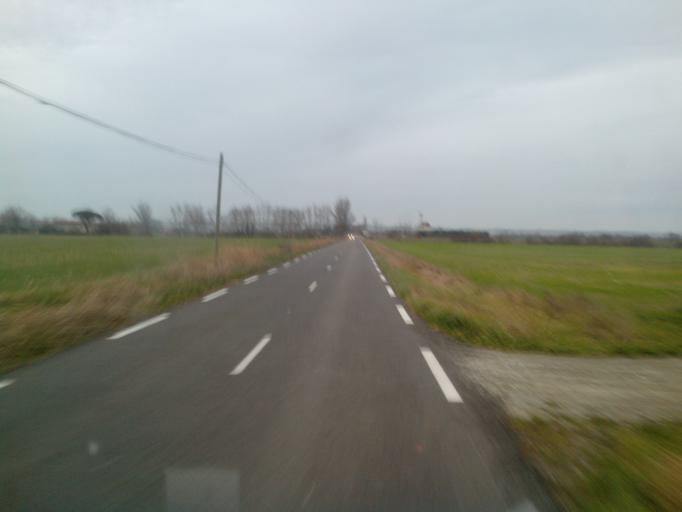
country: FR
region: Midi-Pyrenees
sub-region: Departement de l'Ariege
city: Mazeres
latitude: 43.2296
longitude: 1.6493
